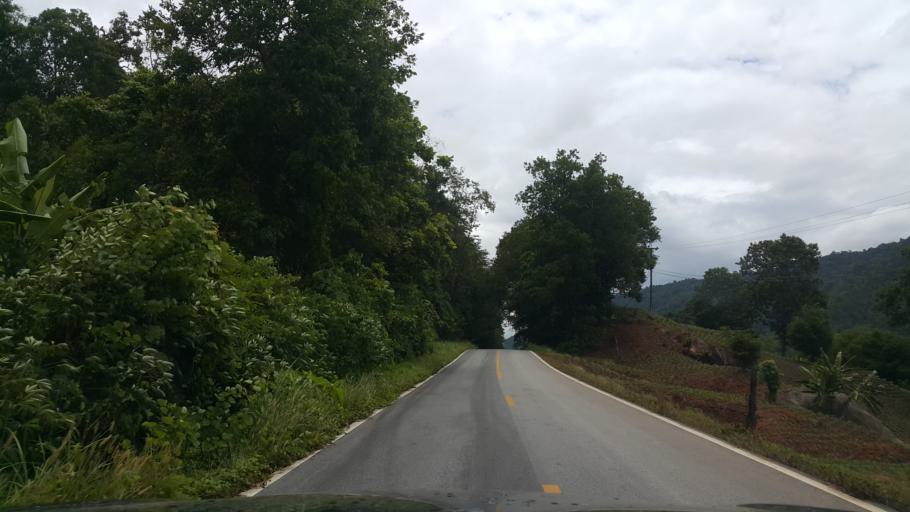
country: TH
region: Phitsanulok
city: Chat Trakan
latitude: 17.3516
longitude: 100.7248
